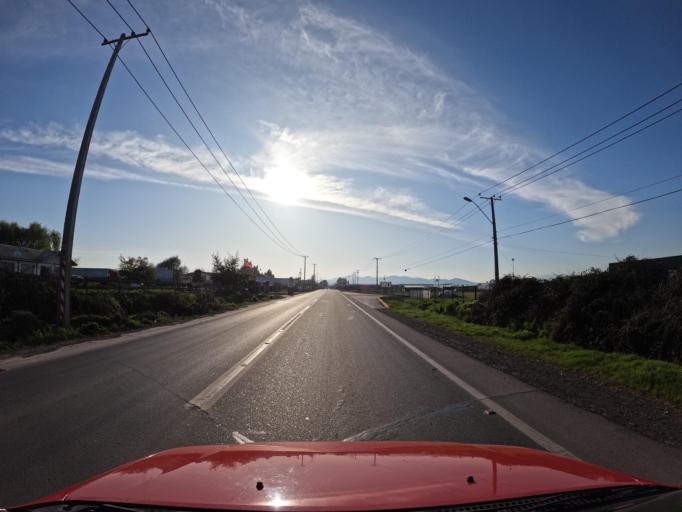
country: CL
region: Maule
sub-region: Provincia de Curico
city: Teno
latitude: -34.8540
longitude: -71.1080
